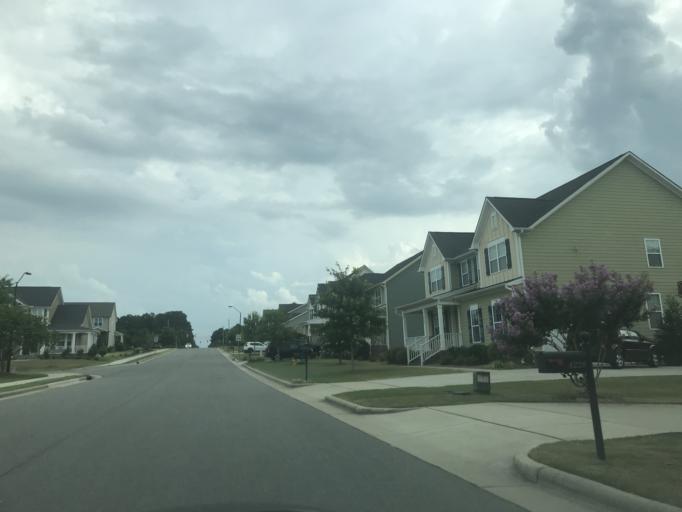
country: US
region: North Carolina
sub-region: Wake County
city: Knightdale
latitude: 35.8362
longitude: -78.5556
